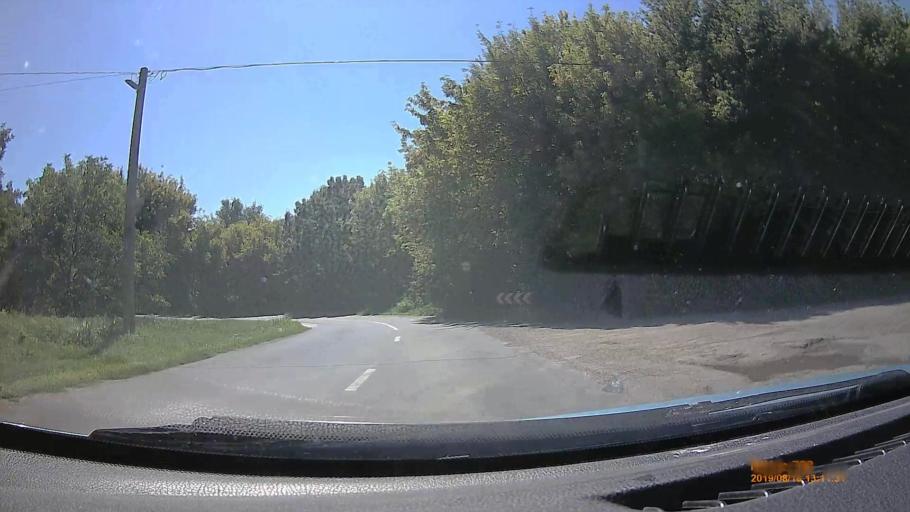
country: HU
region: Fejer
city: Kaloz
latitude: 46.9034
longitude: 18.5187
